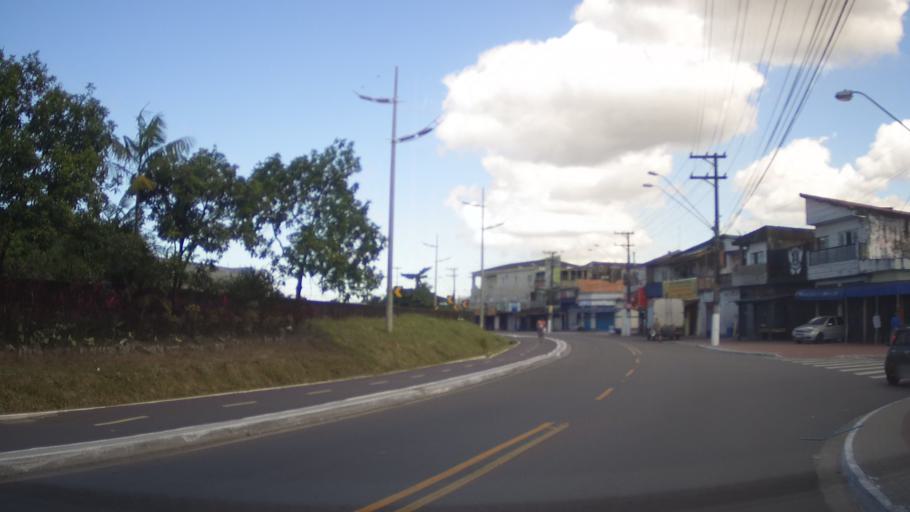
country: BR
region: Sao Paulo
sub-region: Praia Grande
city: Praia Grande
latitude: -24.0311
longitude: -46.5099
